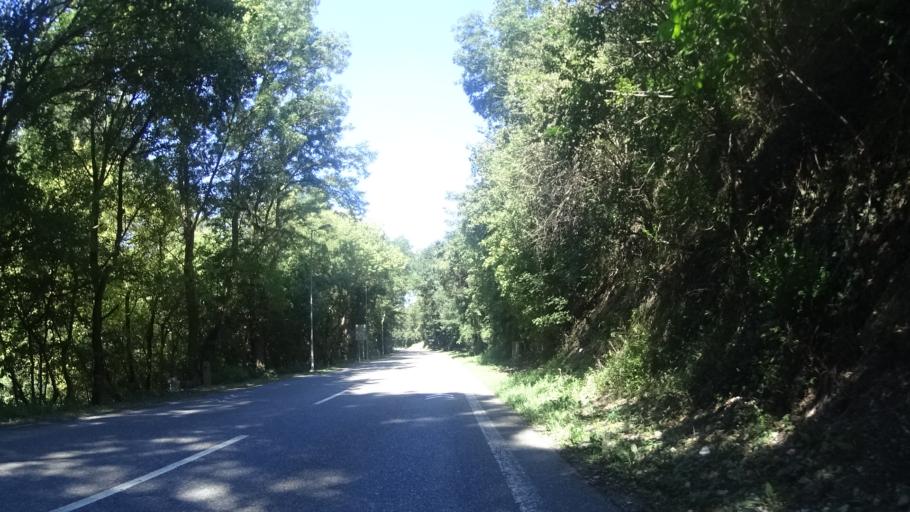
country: AT
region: Lower Austria
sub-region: Politischer Bezirk Bruck an der Leitha
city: Wolfsthal
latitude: 48.1494
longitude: 17.0426
